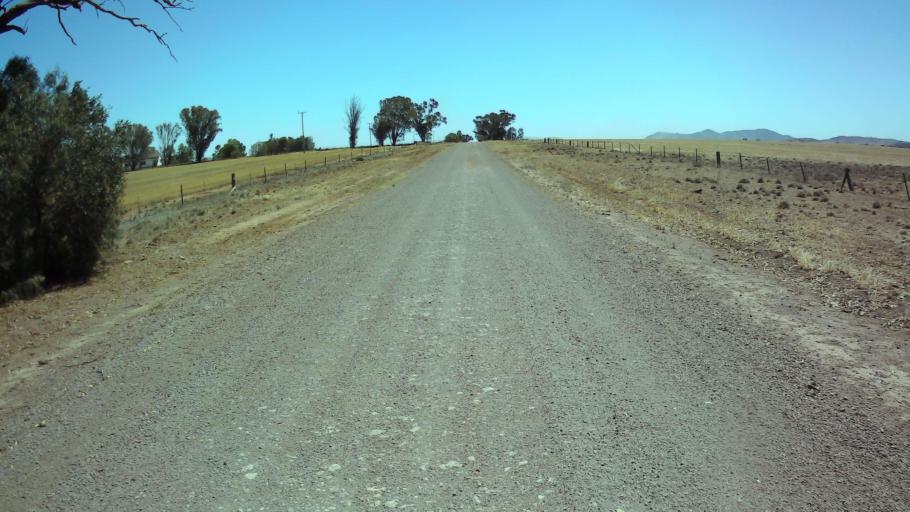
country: AU
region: New South Wales
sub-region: Forbes
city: Forbes
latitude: -33.6981
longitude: 147.7072
